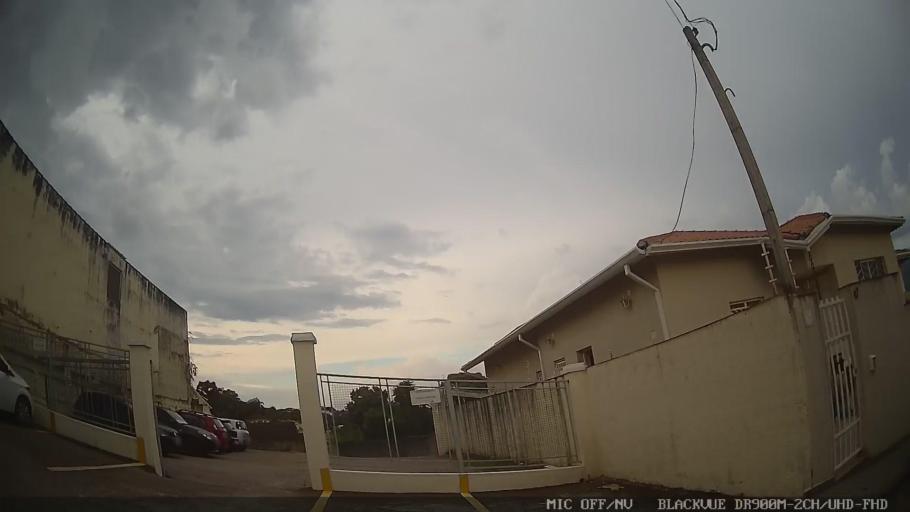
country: BR
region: Sao Paulo
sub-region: Atibaia
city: Atibaia
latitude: -23.1190
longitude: -46.5543
